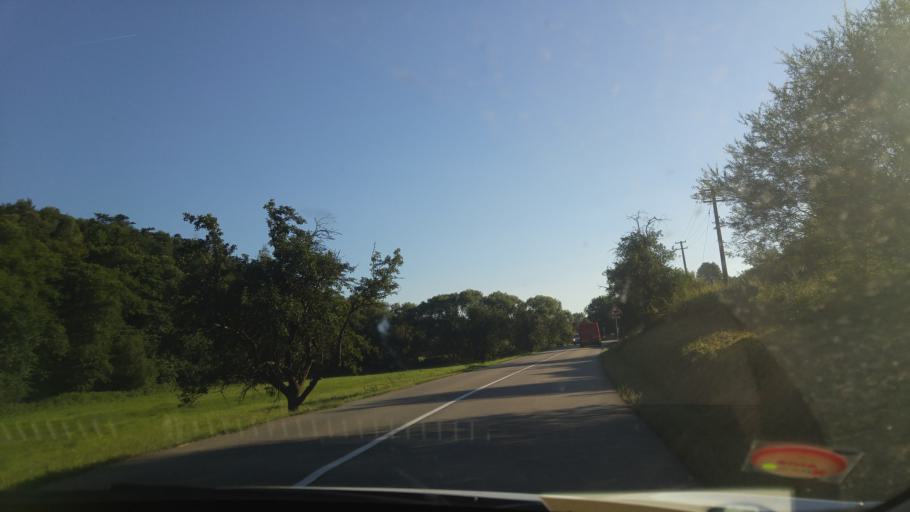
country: CZ
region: South Moravian
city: Veverska Bityska
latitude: 49.2463
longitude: 16.4471
